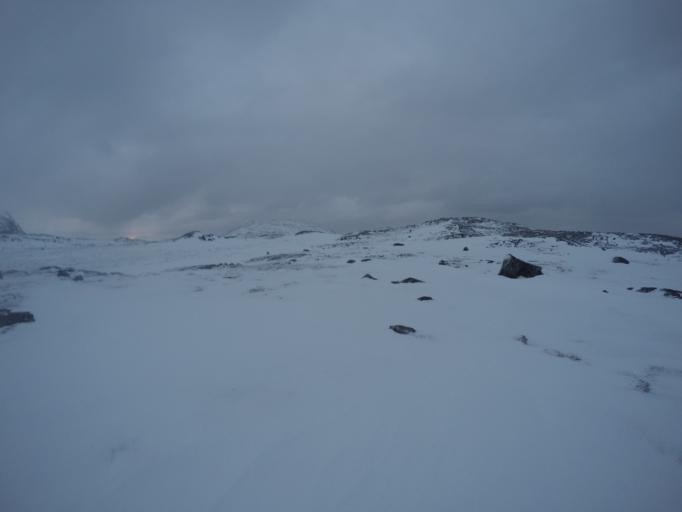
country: GL
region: Sermersooq
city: Nuuk
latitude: 64.1381
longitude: -51.6747
